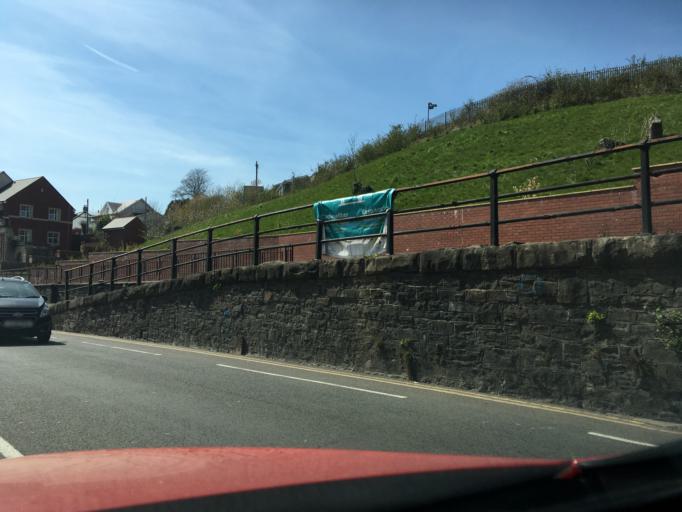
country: GB
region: Wales
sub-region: Merthyr Tydfil County Borough
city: Merthyr Tydfil
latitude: 51.7510
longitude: -3.3757
